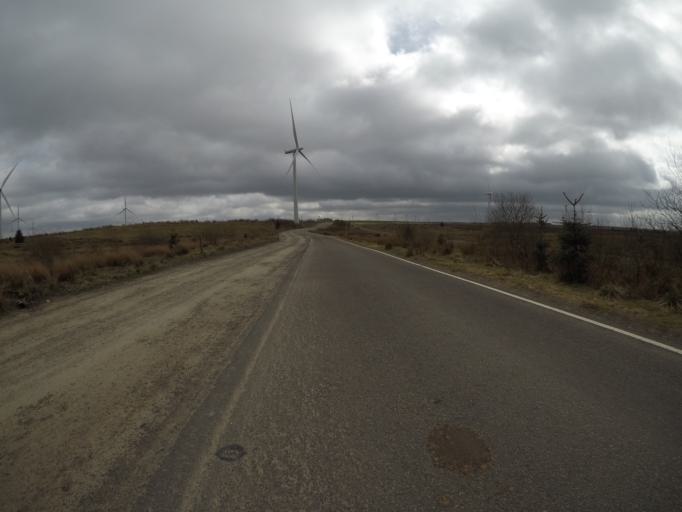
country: GB
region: Scotland
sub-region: East Renfrewshire
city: Newton Mearns
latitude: 55.7023
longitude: -4.3540
